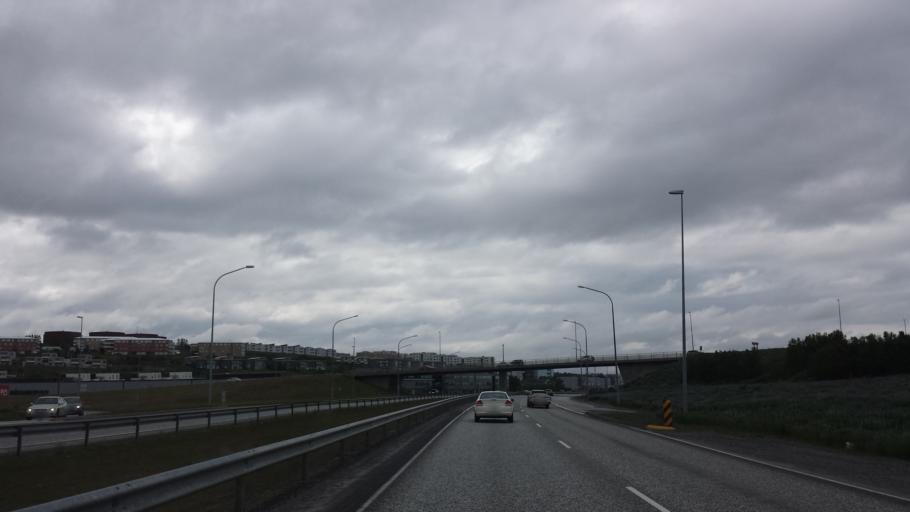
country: IS
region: Capital Region
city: Mosfellsbaer
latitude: 64.1344
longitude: -21.7620
